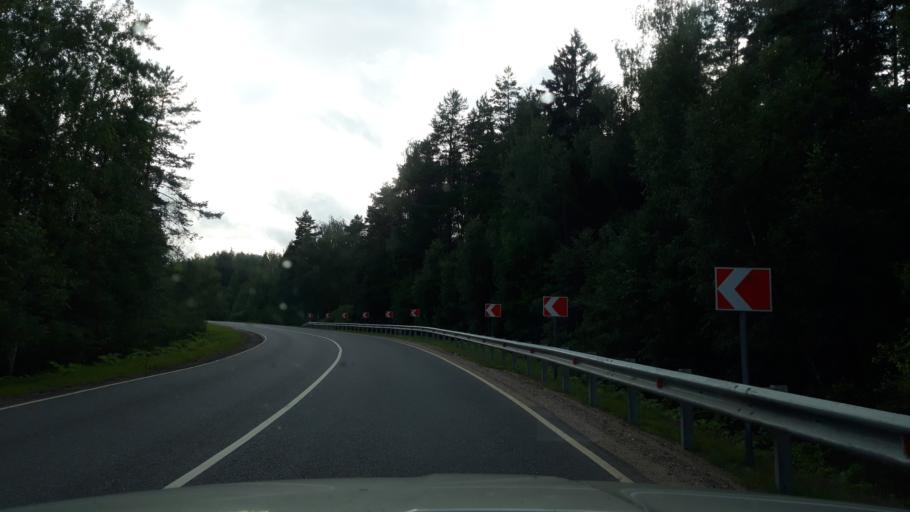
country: RU
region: Moskovskaya
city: Solnechnogorsk
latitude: 56.0963
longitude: 36.8776
